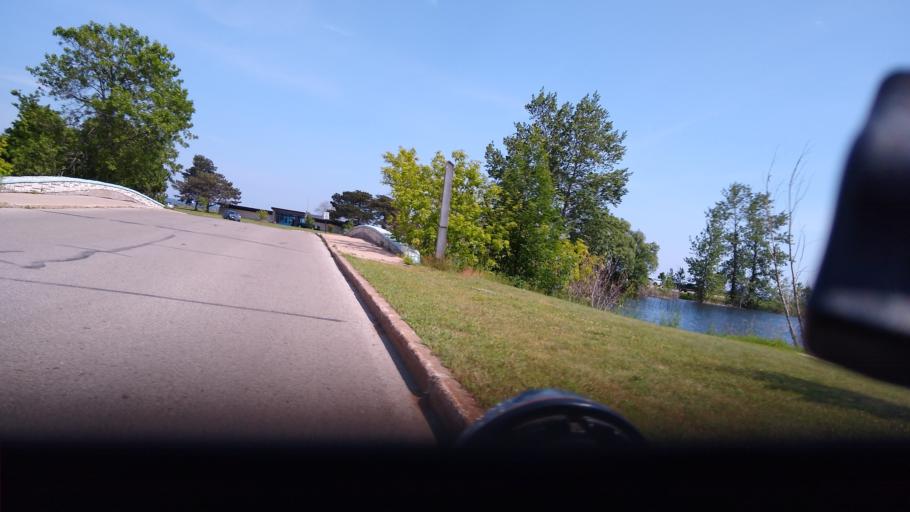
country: US
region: Michigan
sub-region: Delta County
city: Escanaba
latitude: 45.7399
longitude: -87.0491
